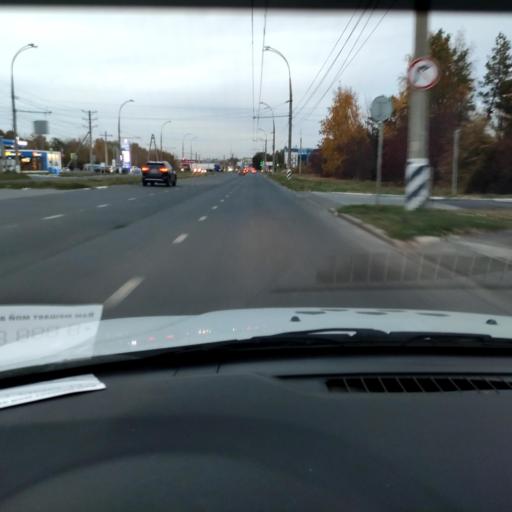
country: RU
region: Samara
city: Tol'yatti
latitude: 53.5491
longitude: 49.3025
